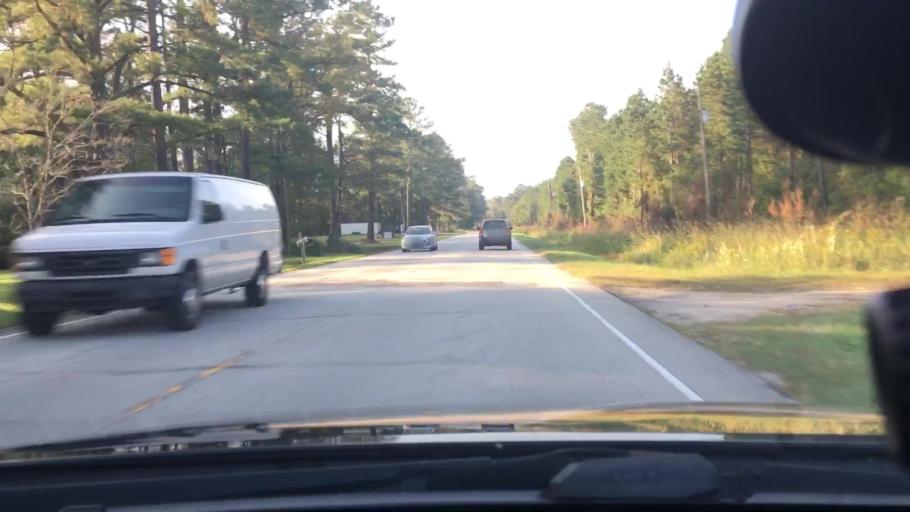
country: US
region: North Carolina
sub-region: Craven County
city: Vanceboro
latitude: 35.4041
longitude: -77.2408
